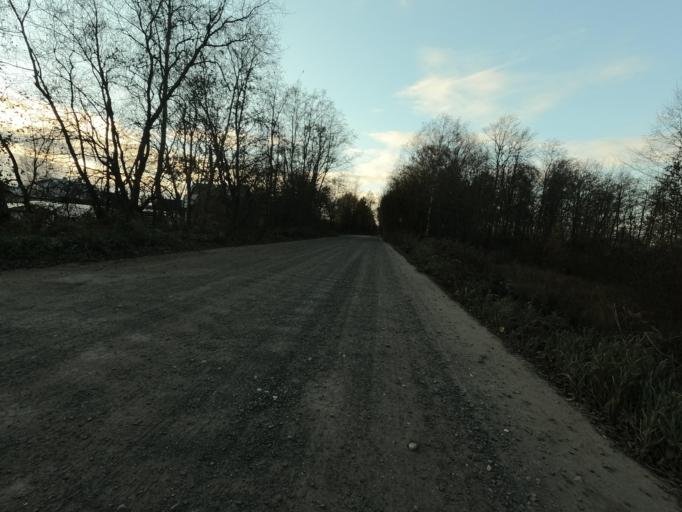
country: RU
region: Leningrad
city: Mga
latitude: 59.7659
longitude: 31.2435
